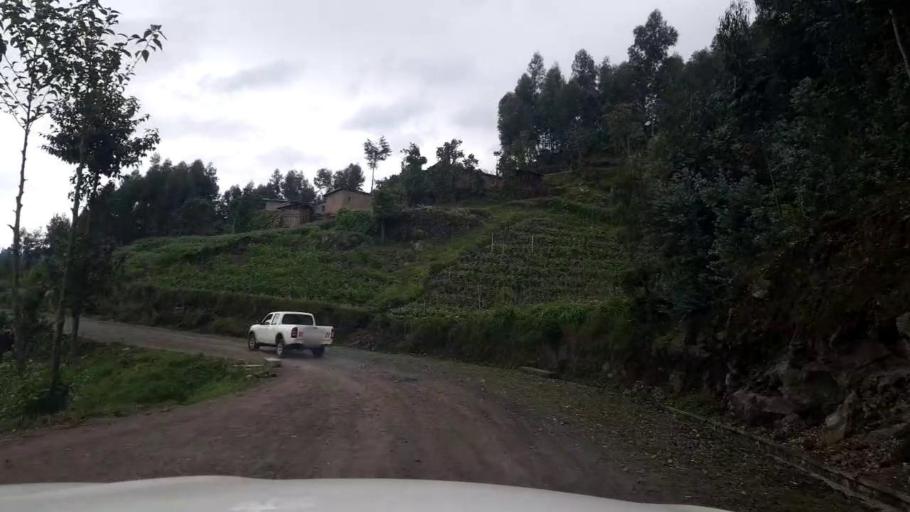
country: RW
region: Northern Province
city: Musanze
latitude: -1.5019
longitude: 29.5336
